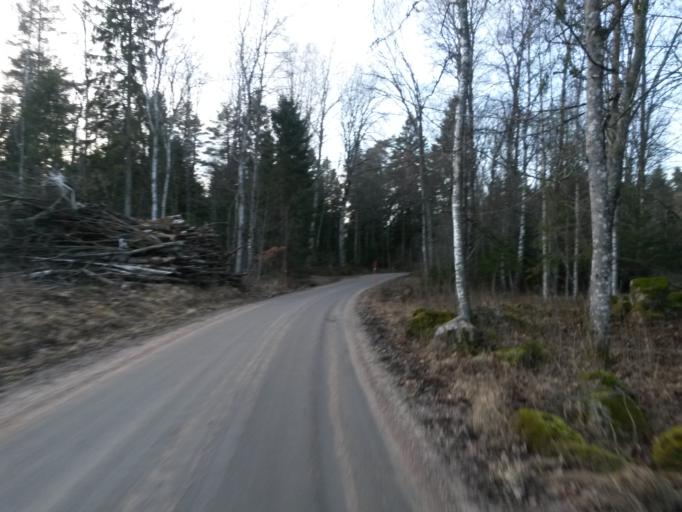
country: SE
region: Vaestra Goetaland
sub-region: Vargarda Kommun
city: Vargarda
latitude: 58.0412
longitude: 12.8438
